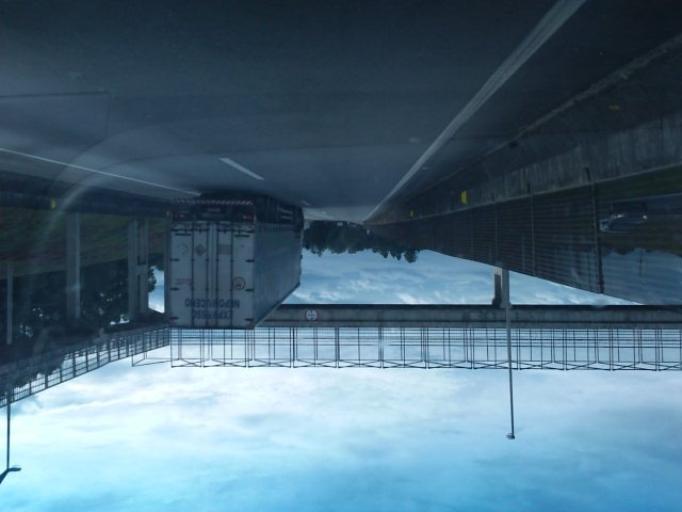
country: BR
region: Parana
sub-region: Quatro Barras
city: Quatro Barras
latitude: -25.3782
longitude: -49.0501
